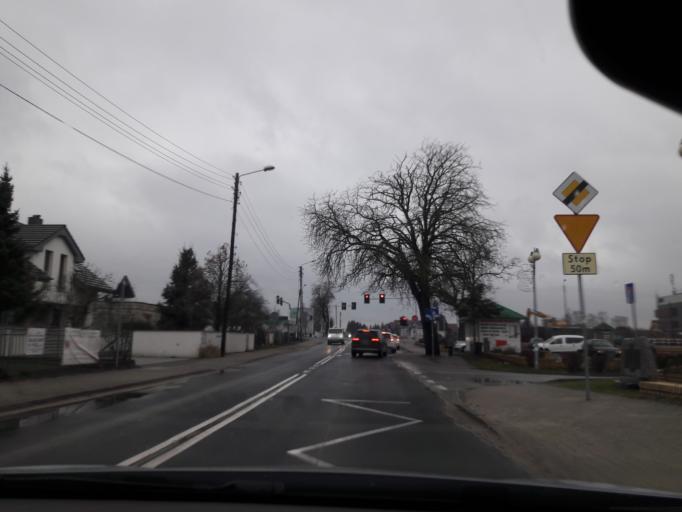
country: PL
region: Greater Poland Voivodeship
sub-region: Powiat poznanski
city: Suchy Las
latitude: 52.4738
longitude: 16.8783
